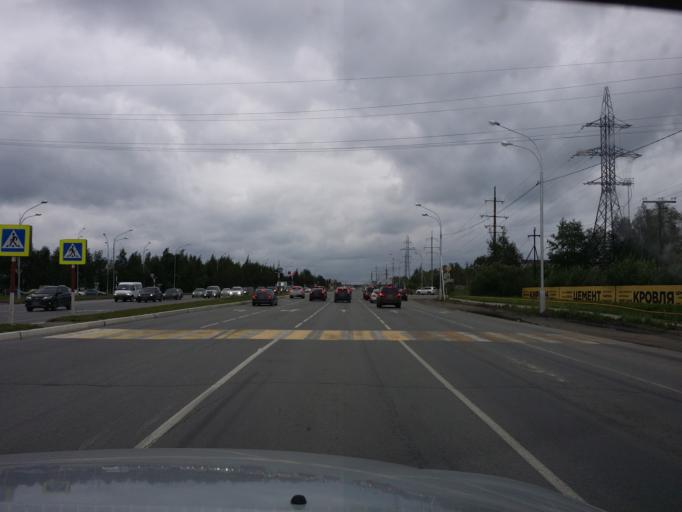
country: RU
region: Khanty-Mansiyskiy Avtonomnyy Okrug
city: Nizhnevartovsk
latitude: 60.9471
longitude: 76.5297
